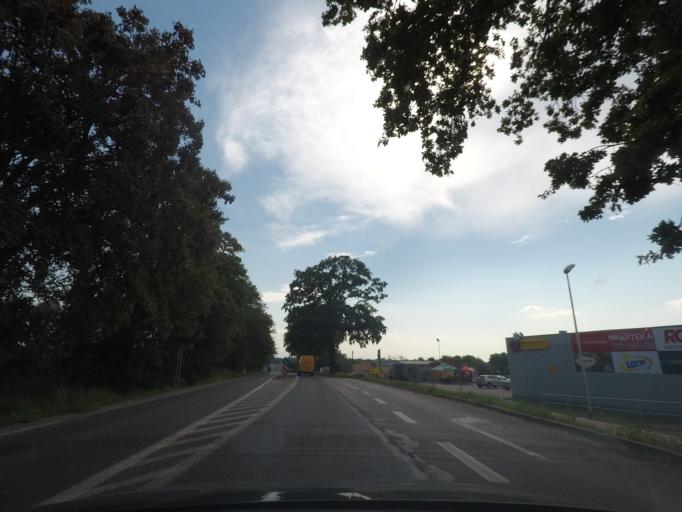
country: PL
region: Lesser Poland Voivodeship
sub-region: Powiat oswiecimski
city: Brzeszcze
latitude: 49.9829
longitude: 19.1540
